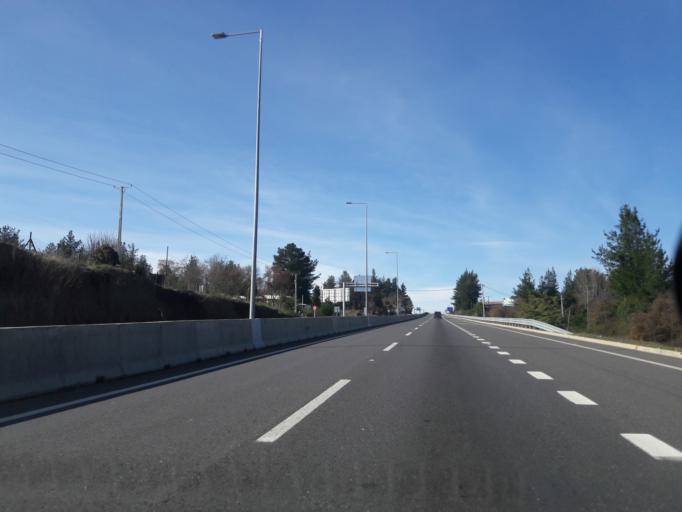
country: CL
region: Biobio
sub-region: Provincia de Biobio
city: Yumbel
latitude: -36.9623
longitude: -72.7167
